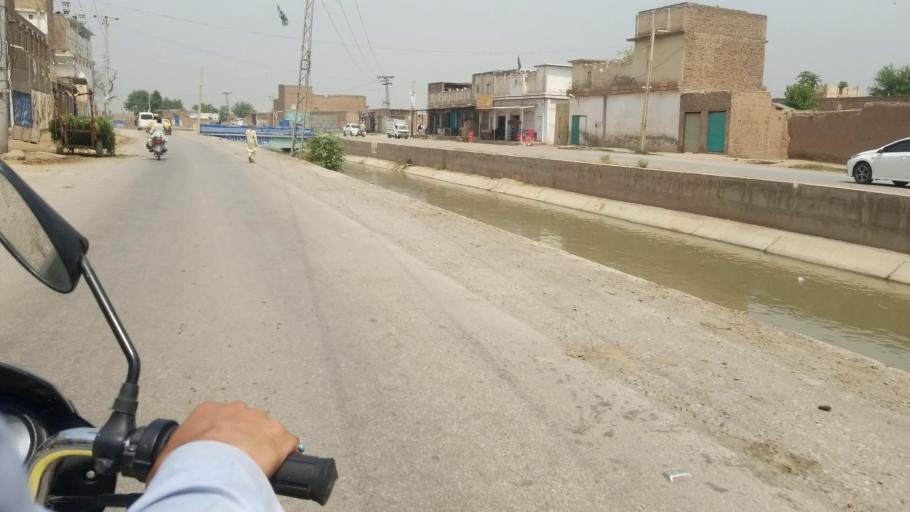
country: PK
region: Khyber Pakhtunkhwa
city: Peshawar
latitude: 33.9557
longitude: 71.5505
